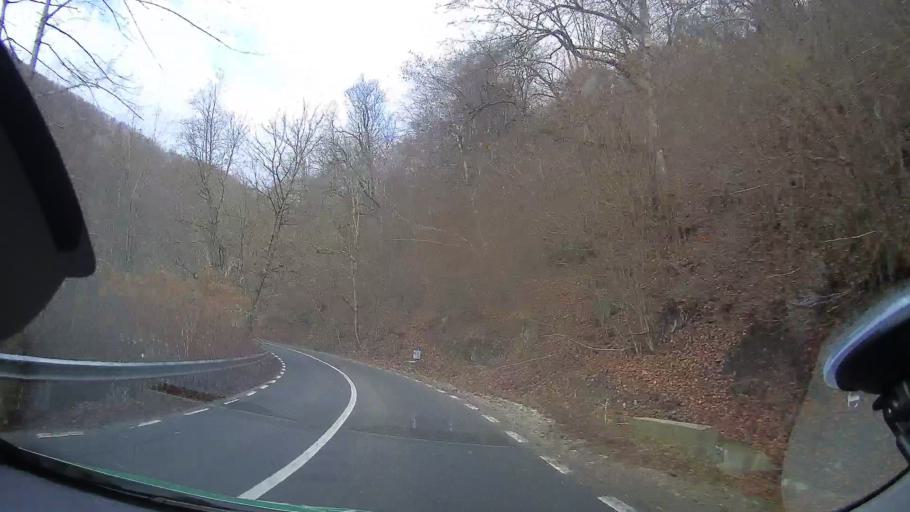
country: RO
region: Cluj
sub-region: Comuna Valea Ierii
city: Valea Ierii
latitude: 46.6321
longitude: 23.3743
